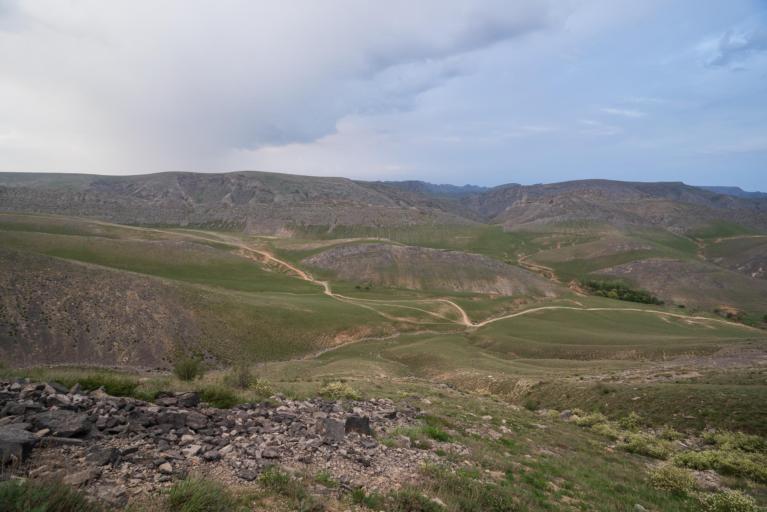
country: KZ
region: Ongtustik Qazaqstan
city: Ashchysay
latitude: 43.5692
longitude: 68.8731
